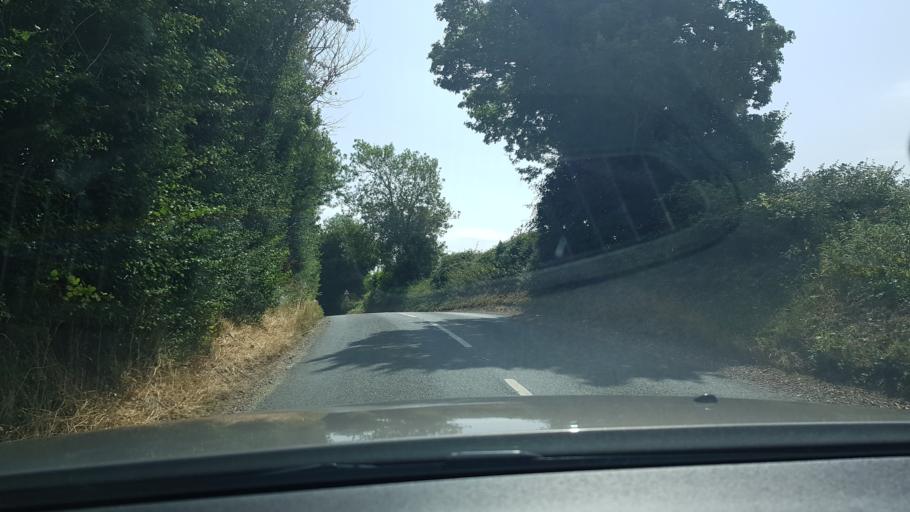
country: GB
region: England
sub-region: West Berkshire
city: Wickham
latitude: 51.4759
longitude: -1.4567
